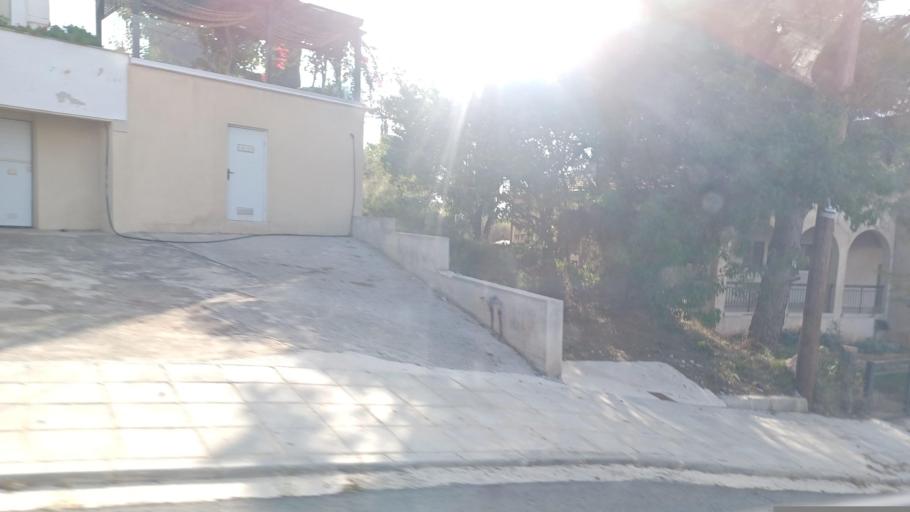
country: CY
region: Pafos
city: Mesogi
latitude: 34.7978
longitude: 32.4870
